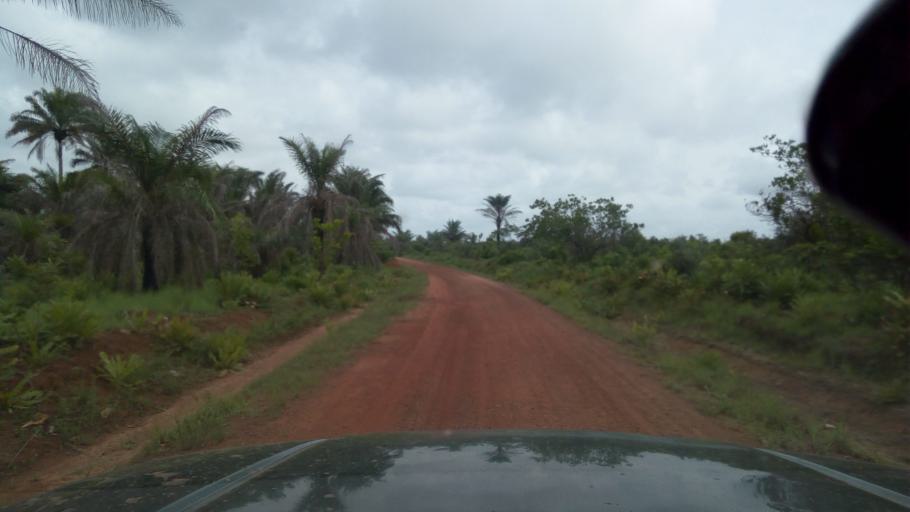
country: SL
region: Northern Province
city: Port Loko
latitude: 8.7683
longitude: -12.9062
